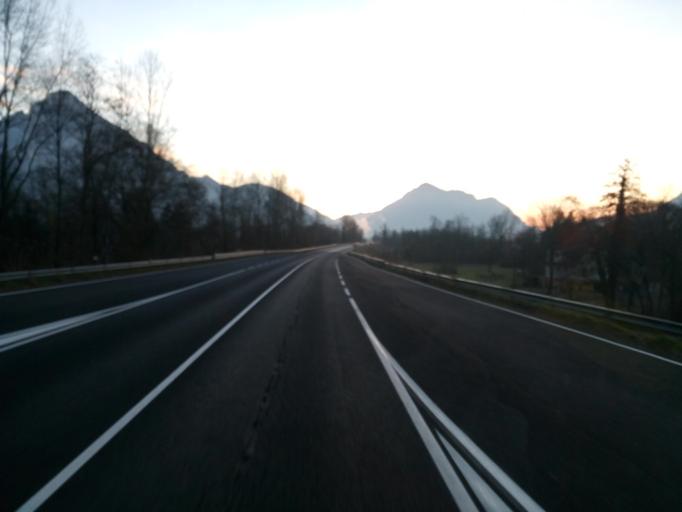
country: IT
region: Friuli Venezia Giulia
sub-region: Provincia di Udine
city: Chiaulis
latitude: 46.4049
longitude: 12.9925
